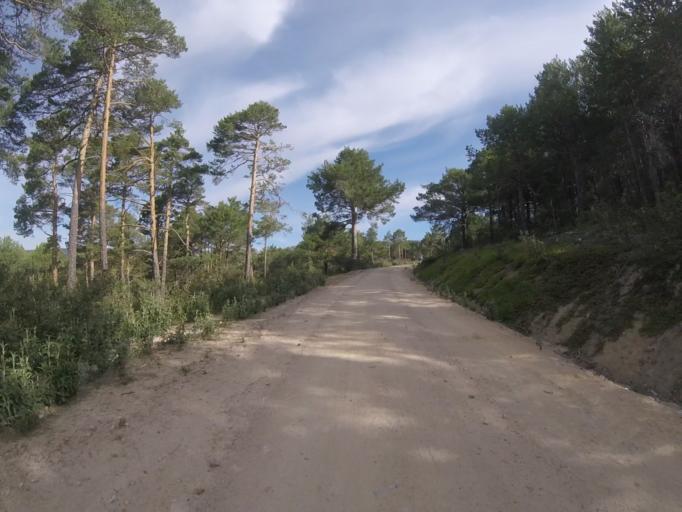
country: ES
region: Castille and Leon
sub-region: Provincia de Avila
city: Peguerinos
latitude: 40.6567
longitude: -4.1856
